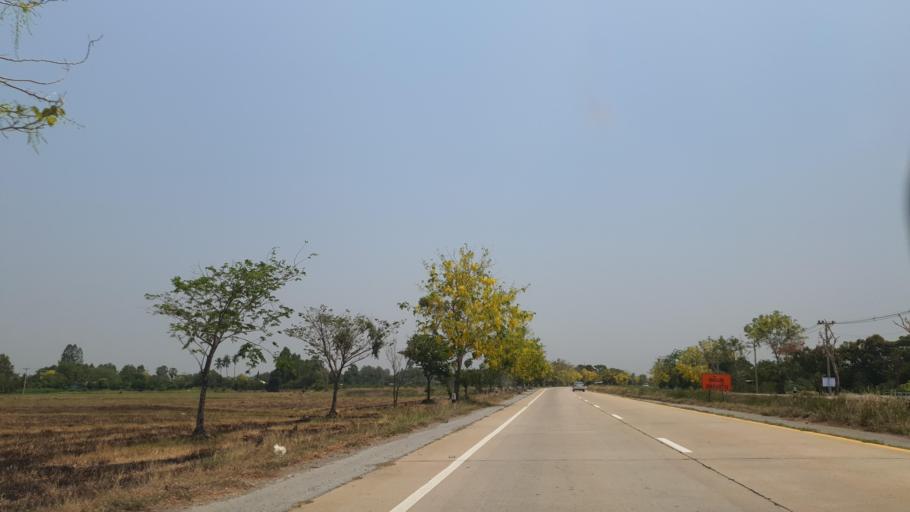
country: TH
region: Suphan Buri
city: Suphan Buri
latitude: 14.5196
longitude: 100.0544
